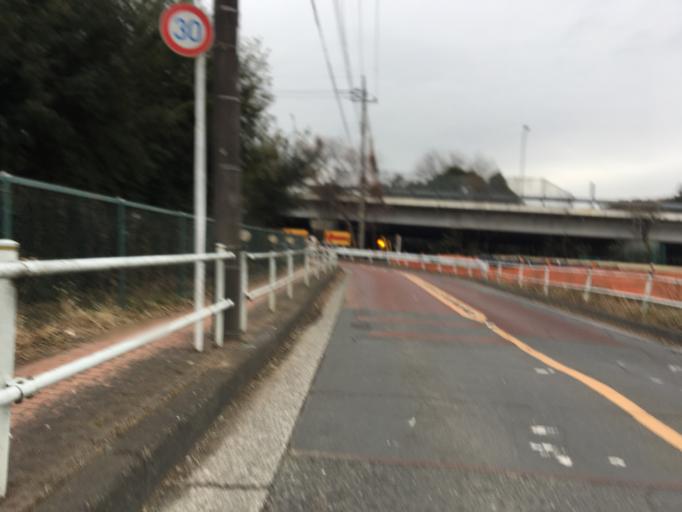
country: JP
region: Saitama
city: Oi
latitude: 35.8029
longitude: 139.5372
